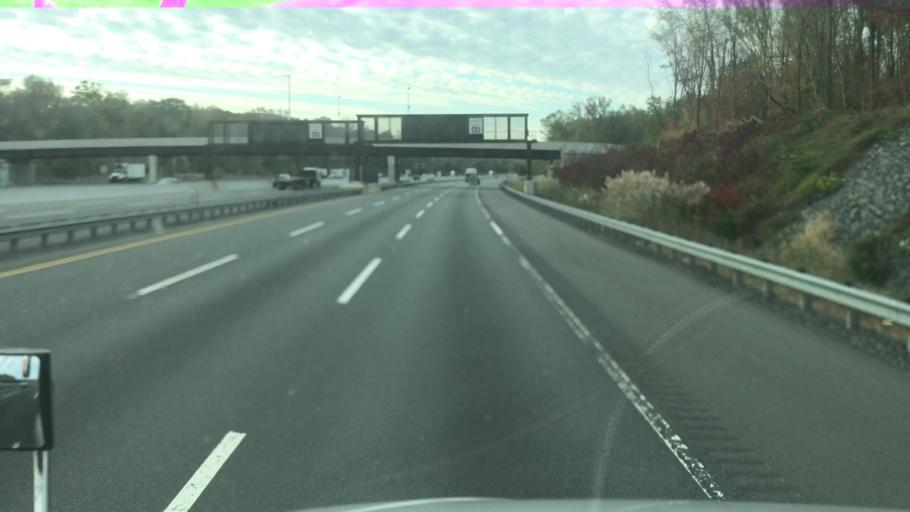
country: US
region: New Jersey
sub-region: Mercer County
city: Hightstown
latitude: 40.2564
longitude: -74.5147
